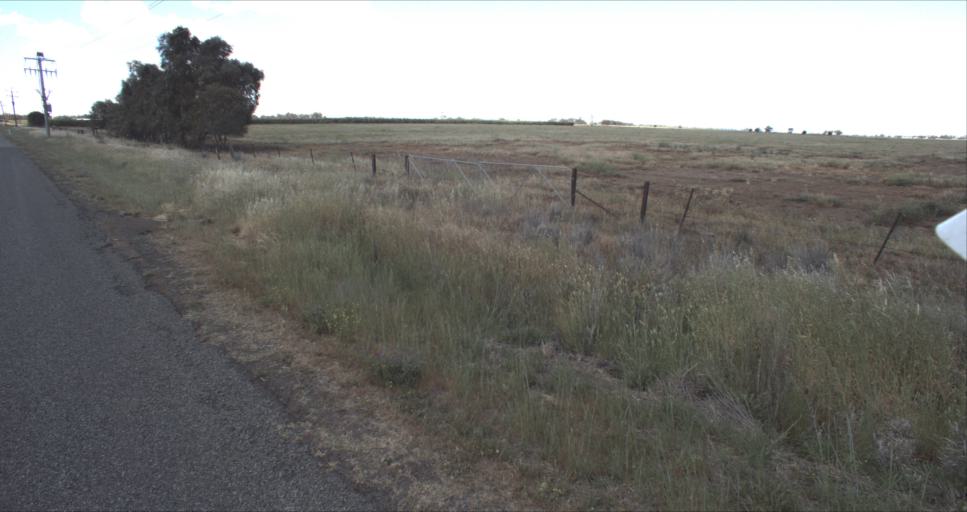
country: AU
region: New South Wales
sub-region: Leeton
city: Leeton
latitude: -34.5271
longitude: 146.2205
